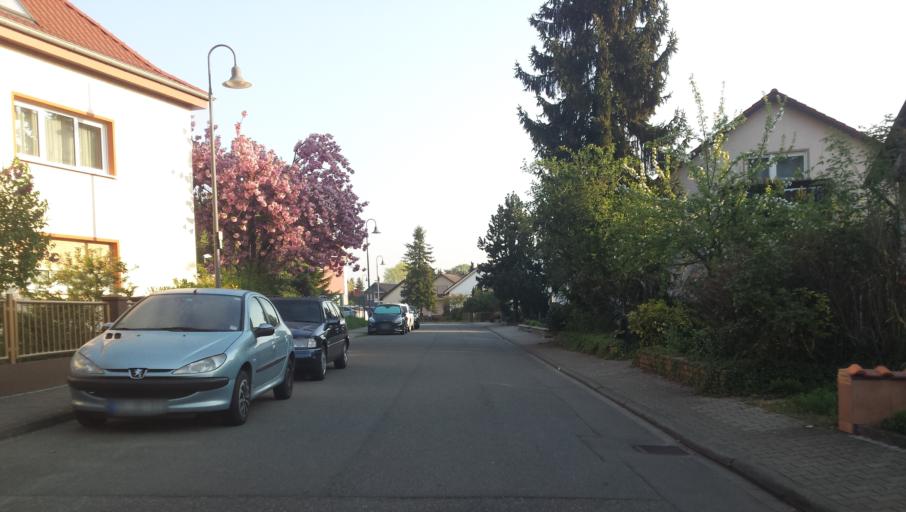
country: DE
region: Baden-Wuerttemberg
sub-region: Karlsruhe Region
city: Bruhl
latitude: 49.3919
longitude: 8.5392
